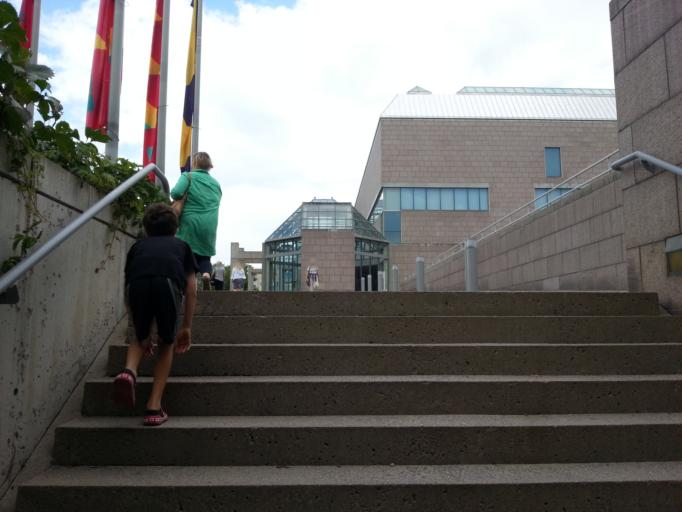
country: CA
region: Ontario
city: Ottawa
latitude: 45.4305
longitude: -75.6985
